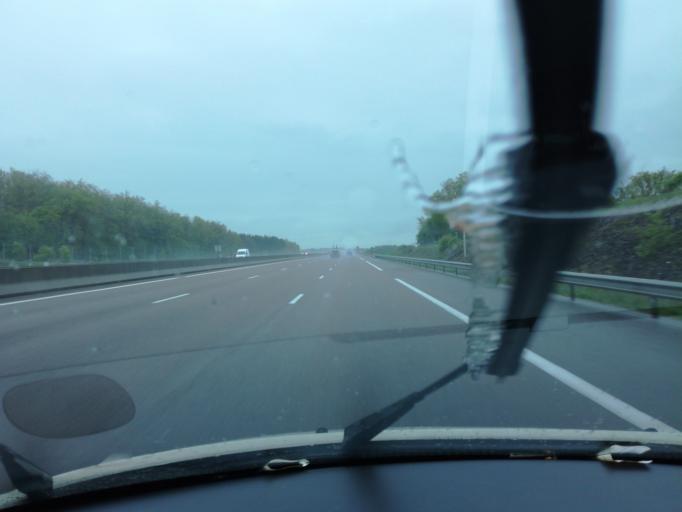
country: FR
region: Champagne-Ardenne
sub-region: Departement de la Haute-Marne
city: Langres
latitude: 47.8551
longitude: 5.2272
